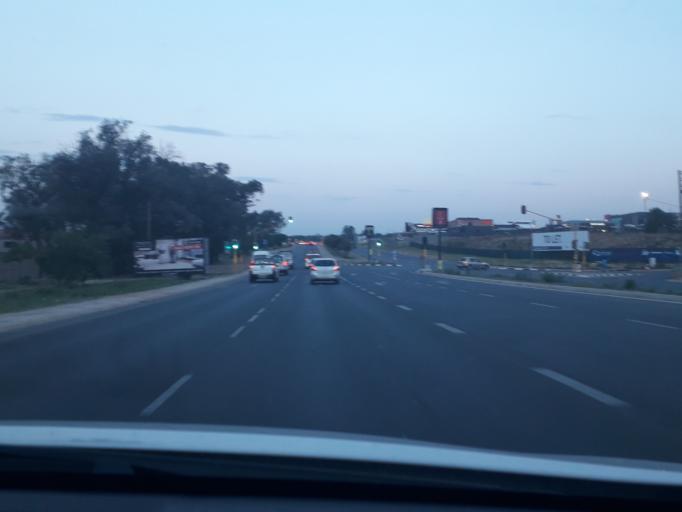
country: ZA
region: Gauteng
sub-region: City of Johannesburg Metropolitan Municipality
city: Midrand
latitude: -25.9833
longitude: 28.0701
